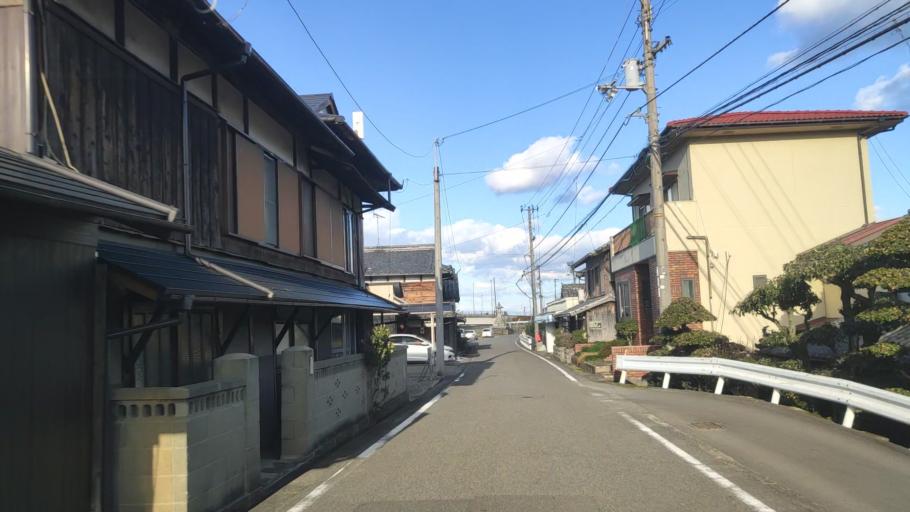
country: JP
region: Ehime
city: Saijo
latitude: 33.9094
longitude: 133.1313
